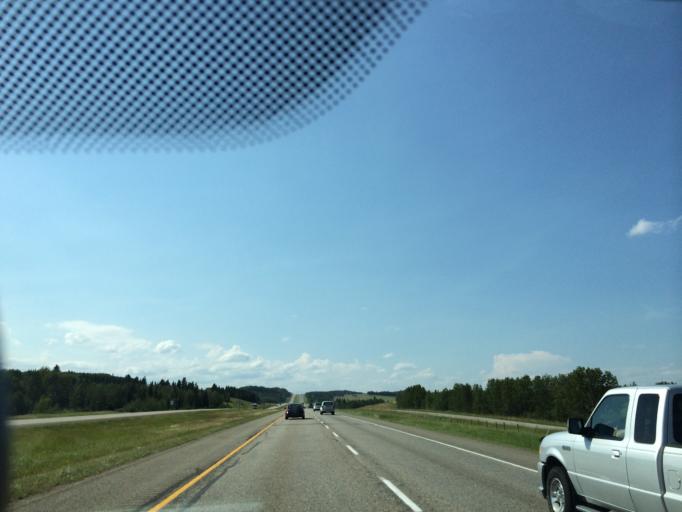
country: CA
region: Alberta
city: Cochrane
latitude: 51.1246
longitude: -114.6772
